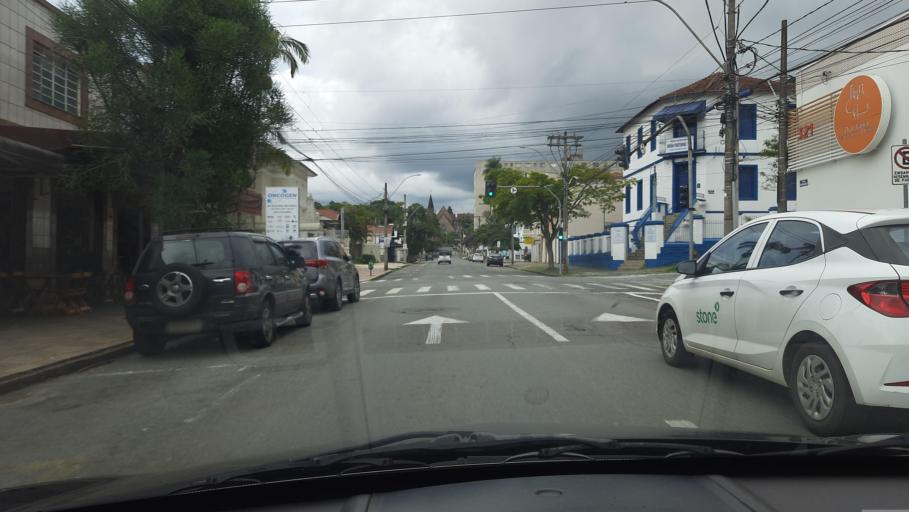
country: BR
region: Minas Gerais
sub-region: Pocos De Caldas
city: Pocos de Caldas
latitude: -21.7829
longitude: -46.5699
